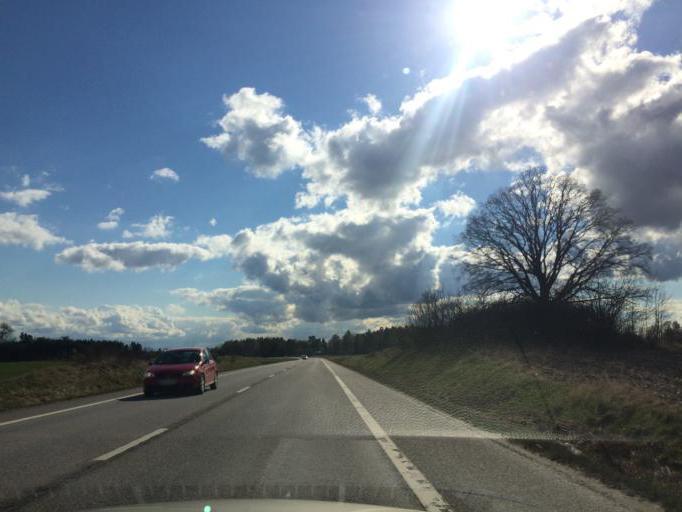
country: SE
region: Soedermanland
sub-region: Eskilstuna Kommun
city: Eskilstuna
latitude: 59.4173
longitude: 16.5913
